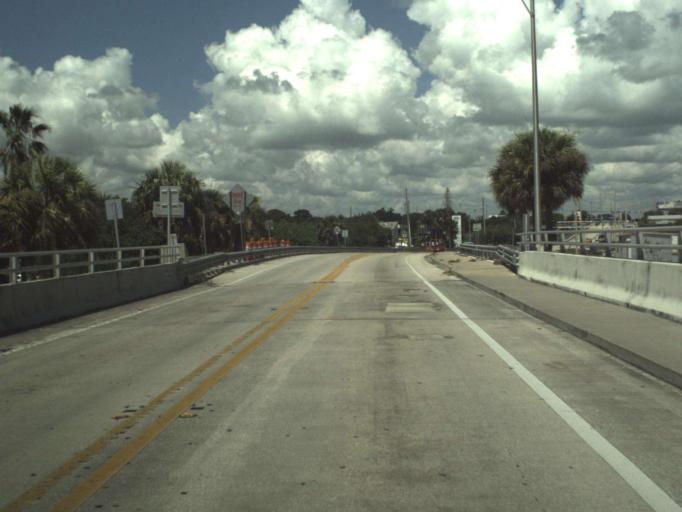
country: US
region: Florida
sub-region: Saint Lucie County
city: Fort Pierce
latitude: 27.4707
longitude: -80.3282
